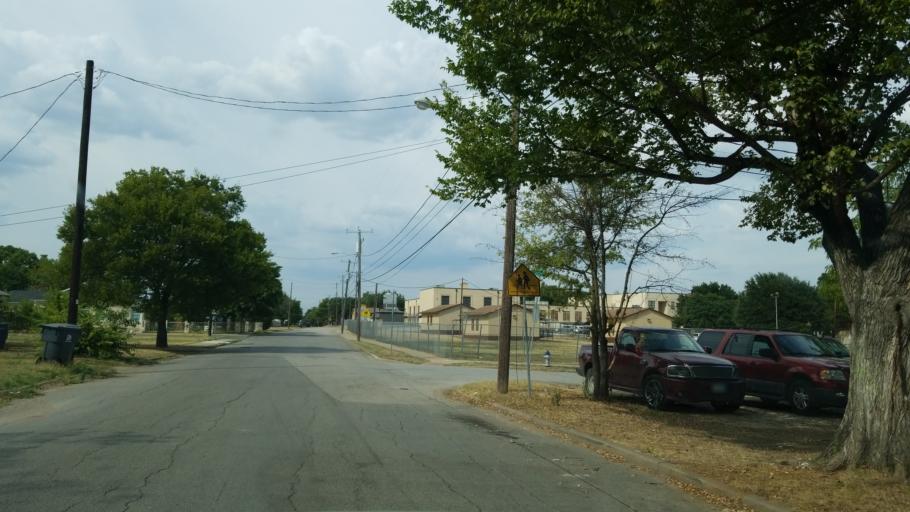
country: US
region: Texas
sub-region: Dallas County
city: Dallas
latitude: 32.7672
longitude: -96.8448
